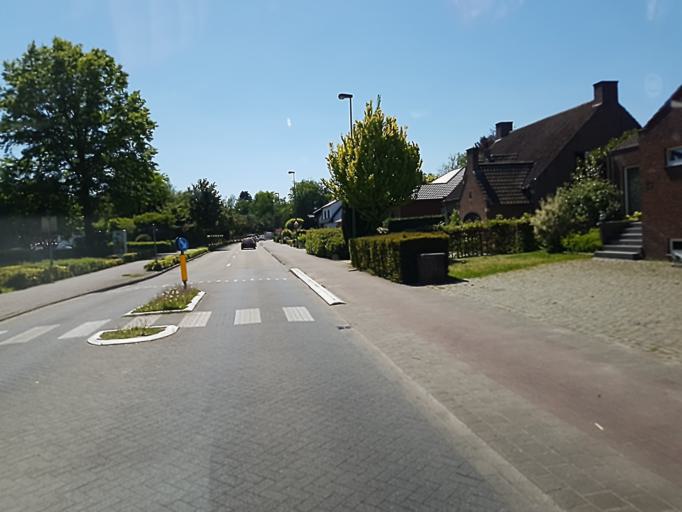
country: BE
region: Flanders
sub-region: Provincie Antwerpen
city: Turnhout
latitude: 51.3079
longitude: 4.9389
